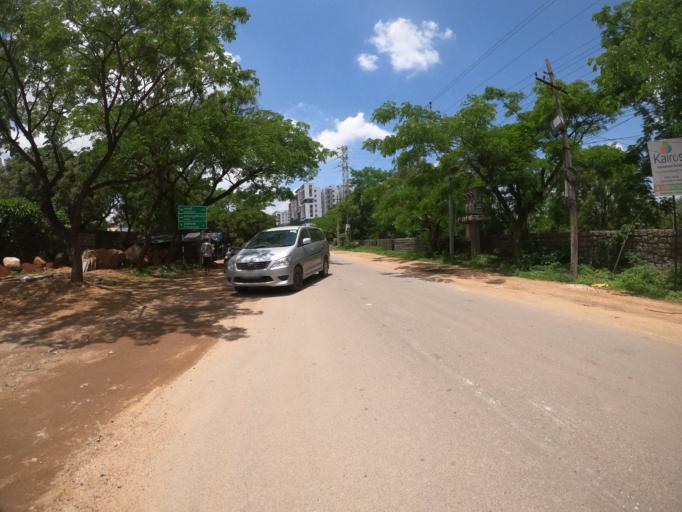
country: IN
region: Telangana
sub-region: Medak
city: Serilingampalle
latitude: 17.3844
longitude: 78.3254
